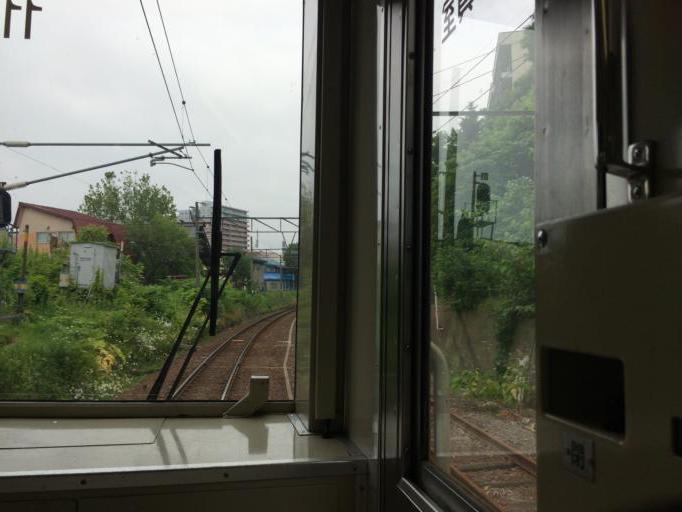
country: JP
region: Hokkaido
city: Otaru
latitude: 43.2009
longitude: 140.9914
